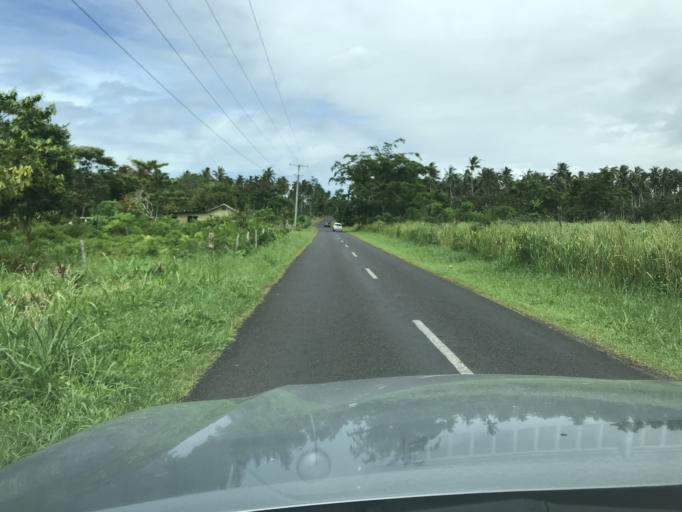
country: WS
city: Nofoali`i
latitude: -13.8735
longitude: -171.9239
